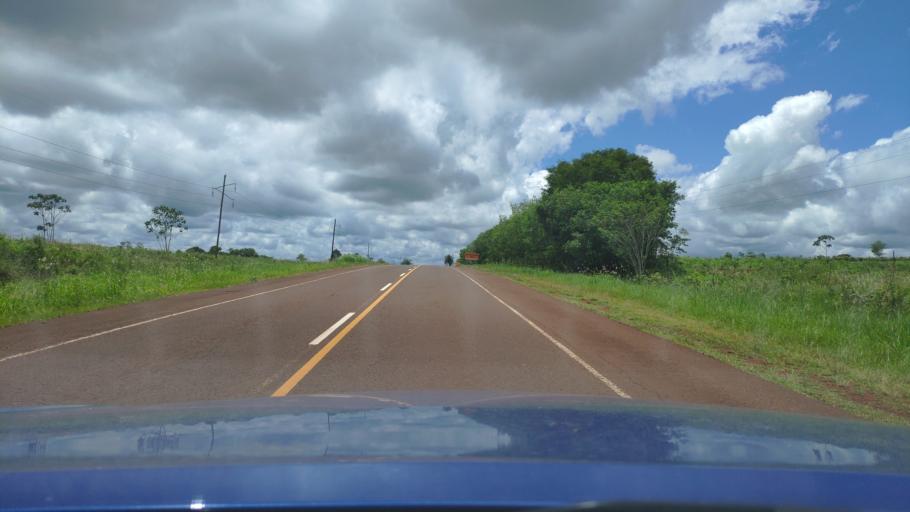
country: AR
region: Misiones
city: Picada Gobernador Lopez
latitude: -27.6733
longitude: -55.2798
